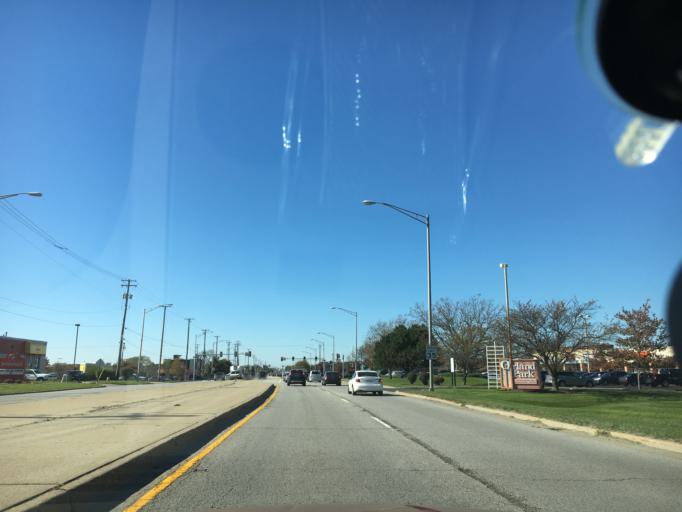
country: US
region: Illinois
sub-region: Cook County
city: Tinley Park
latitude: 41.6024
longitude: -87.7891
